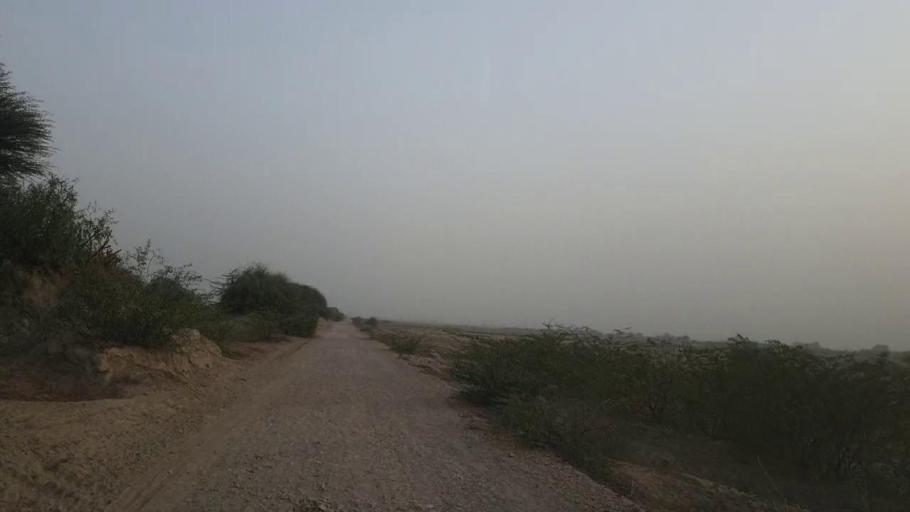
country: PK
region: Sindh
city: Kunri
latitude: 25.1185
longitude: 69.5515
